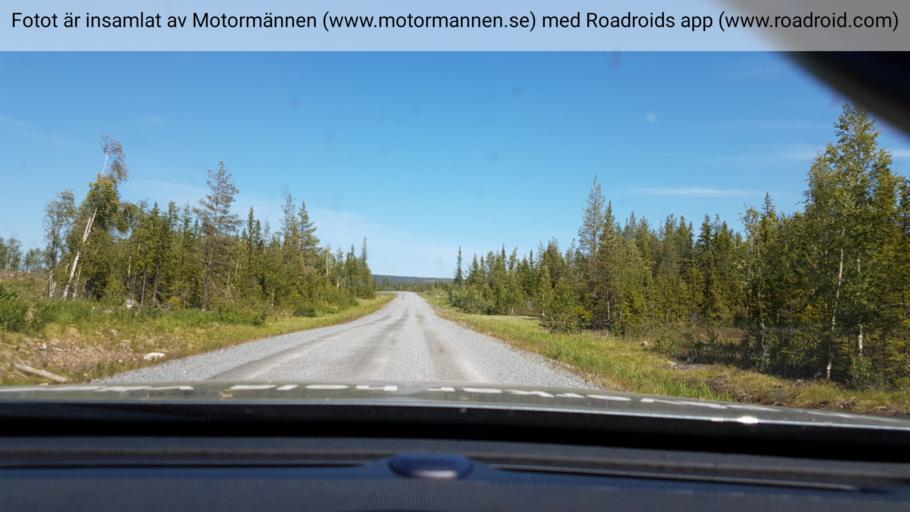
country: SE
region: Vaesterbotten
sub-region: Vilhelmina Kommun
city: Sjoberg
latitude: 64.7043
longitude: 15.7618
